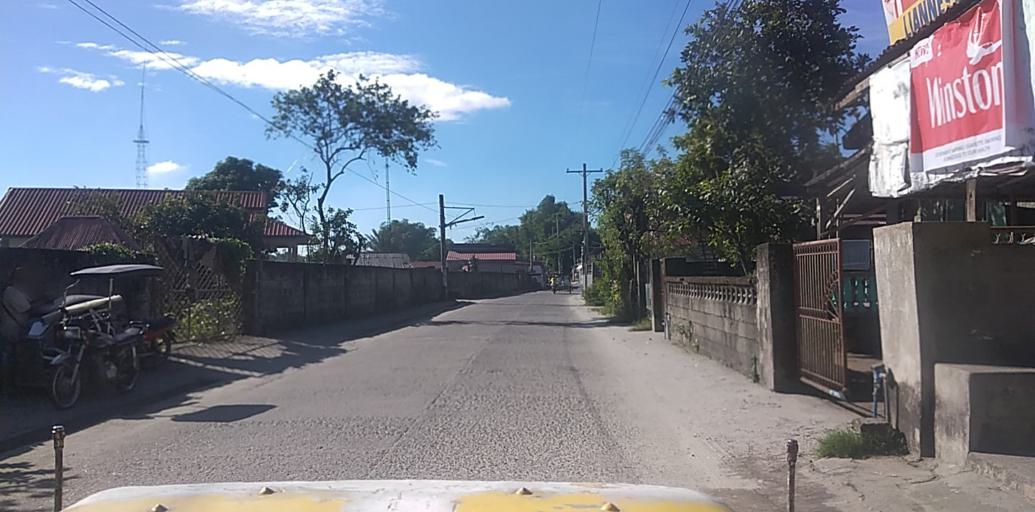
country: PH
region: Central Luzon
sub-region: Province of Pampanga
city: San Patricio
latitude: 15.0933
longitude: 120.7132
